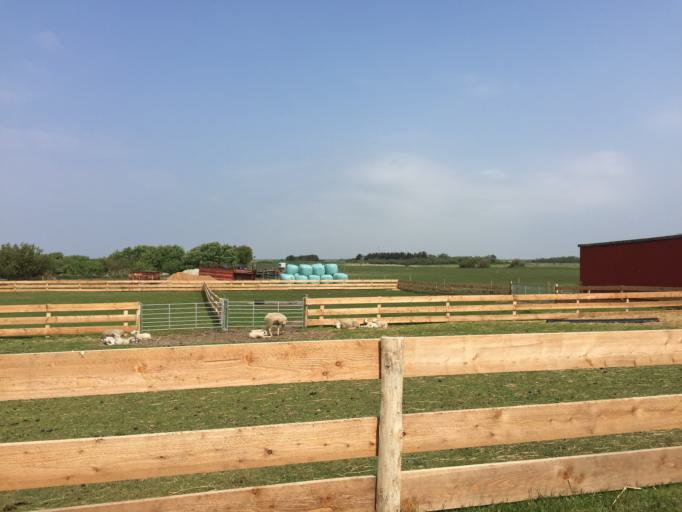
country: DK
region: South Denmark
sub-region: Esbjerg Kommune
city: Tjaereborg
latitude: 55.2818
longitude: 8.5449
